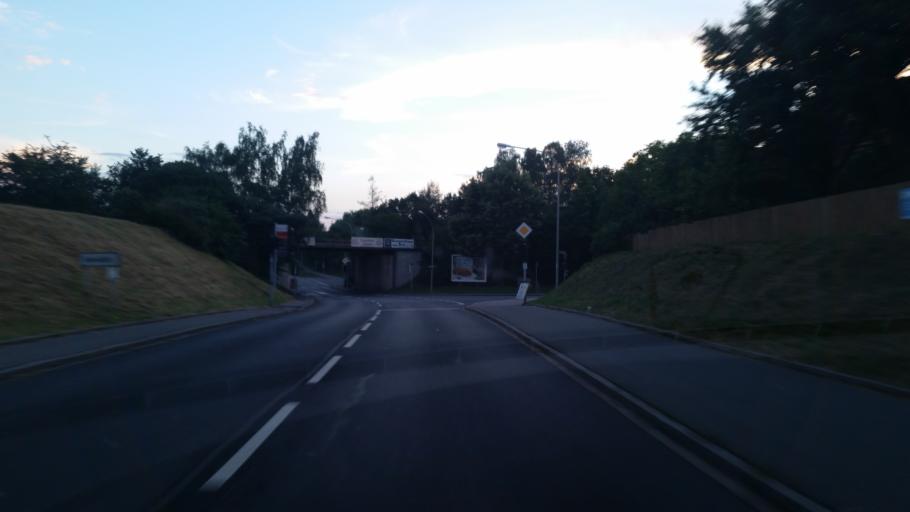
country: DE
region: Bavaria
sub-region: Upper Palatinate
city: Wernberg-Koblitz
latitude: 49.5366
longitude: 12.1507
